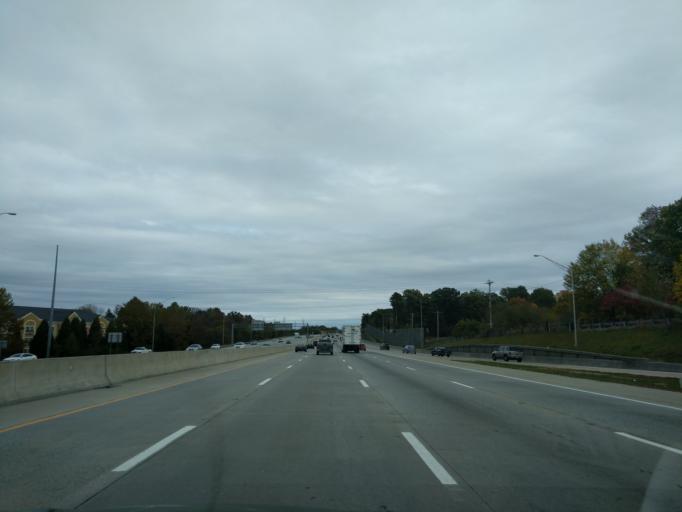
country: US
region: North Carolina
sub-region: Rowan County
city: Salisbury
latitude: 35.6585
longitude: -80.4578
